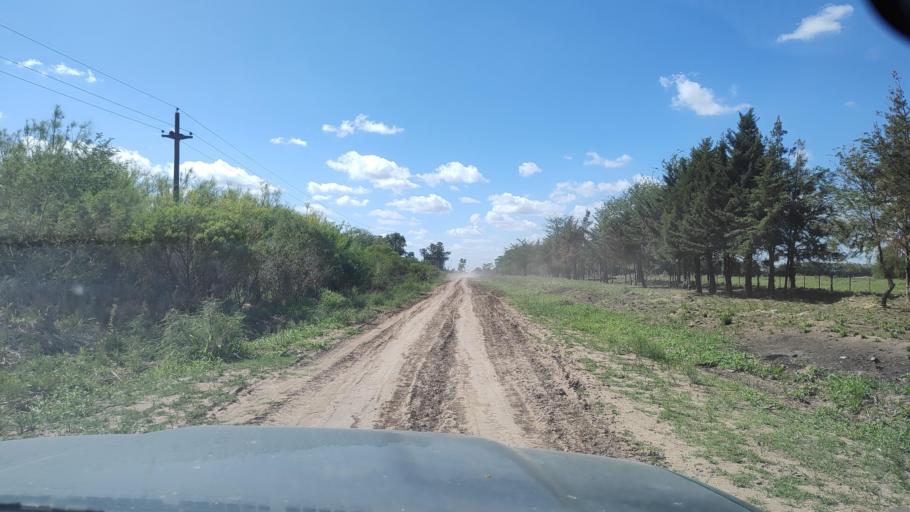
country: AR
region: Buenos Aires
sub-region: Partido de Lujan
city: Lujan
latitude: -34.5330
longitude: -59.1491
